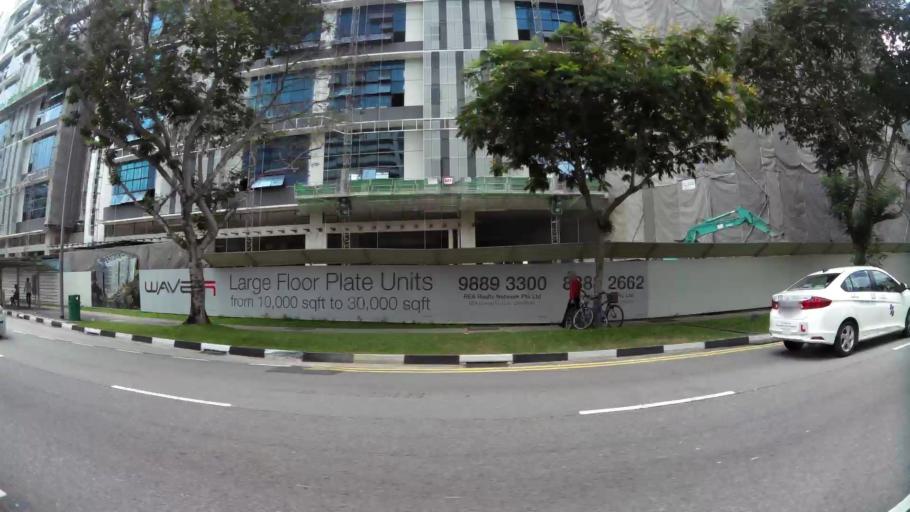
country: MY
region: Johor
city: Johor Bahru
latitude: 1.4481
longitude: 103.7982
